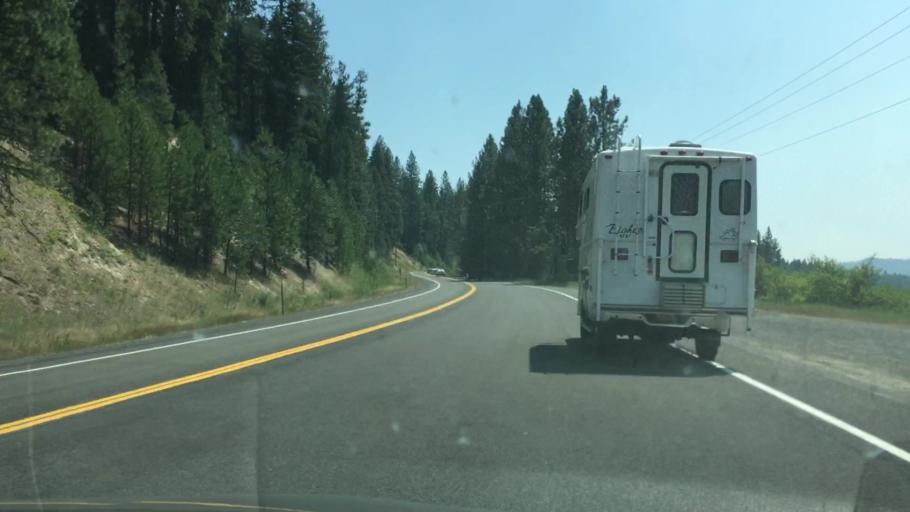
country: US
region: Idaho
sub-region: Valley County
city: McCall
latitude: 45.1144
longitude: -116.3030
